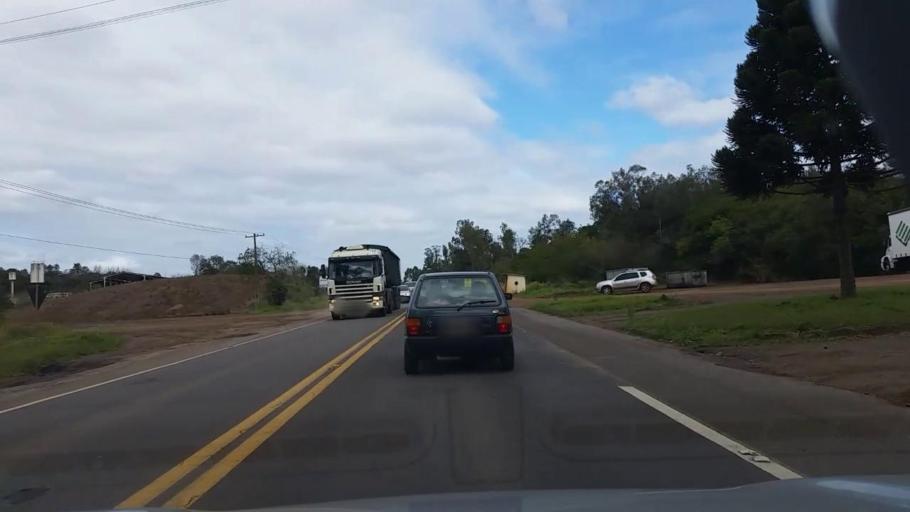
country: BR
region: Rio Grande do Sul
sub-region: Lajeado
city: Lajeado
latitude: -29.4218
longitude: -52.0220
